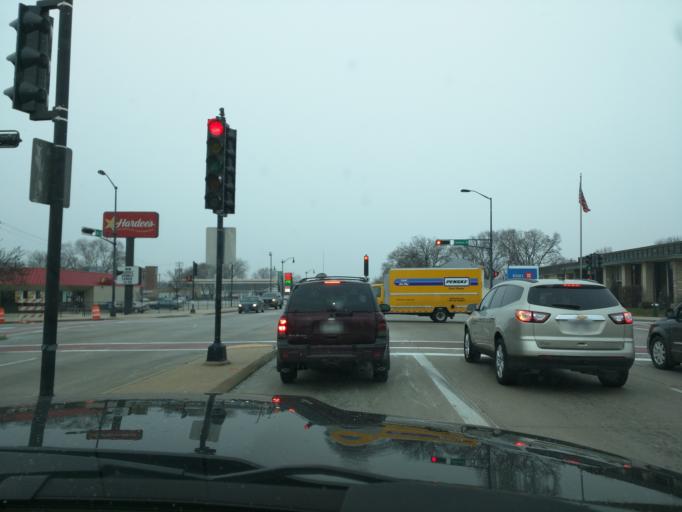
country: US
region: Wisconsin
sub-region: La Crosse County
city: North La Crosse
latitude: 43.8411
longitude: -91.2482
